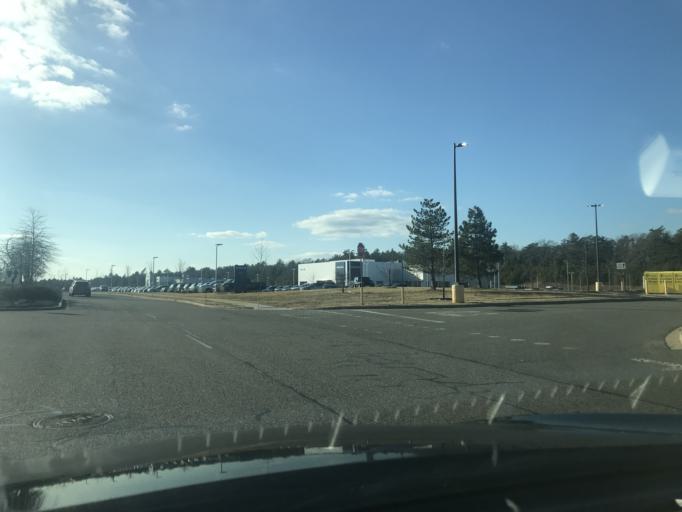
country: US
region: Massachusetts
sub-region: Plymouth County
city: North Plymouth
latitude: 41.9539
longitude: -70.7180
